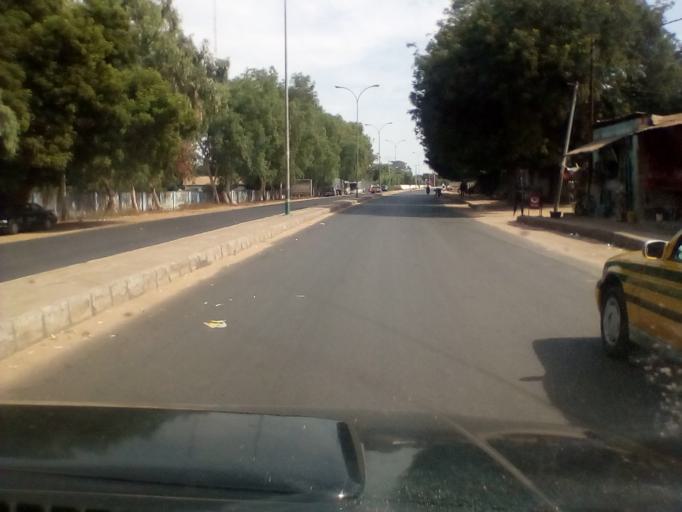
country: GM
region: Western
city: Abuko
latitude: 13.4019
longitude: -16.6562
